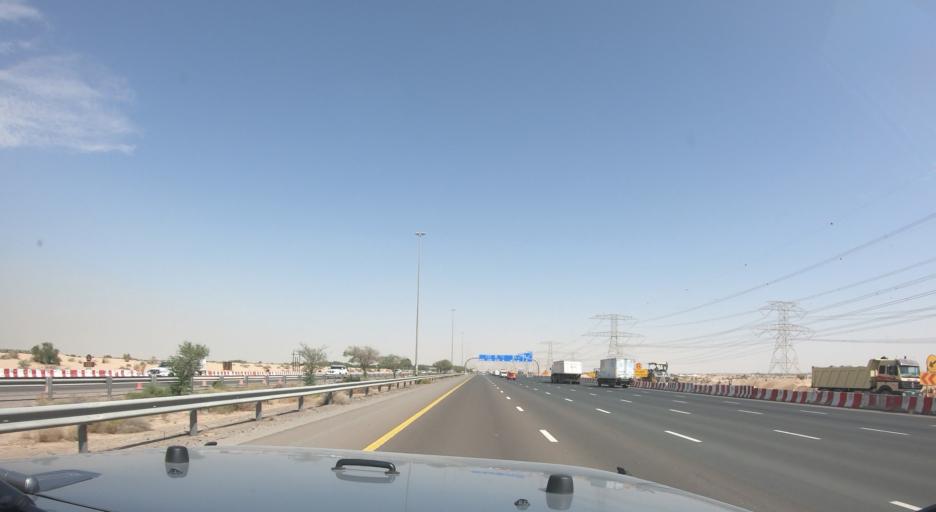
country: AE
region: Ash Shariqah
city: Sharjah
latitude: 25.1819
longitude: 55.5206
